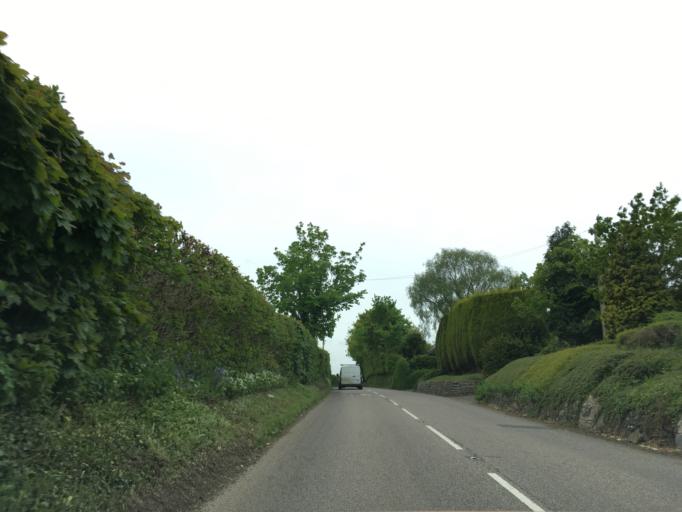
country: GB
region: England
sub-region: South Gloucestershire
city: Almondsbury
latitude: 51.5492
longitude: -2.5797
